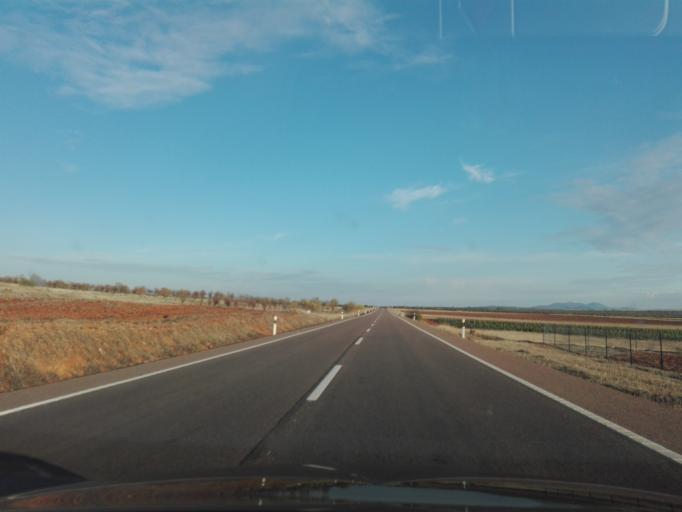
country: ES
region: Extremadura
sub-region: Provincia de Badajoz
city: Usagre
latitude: 38.3561
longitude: -6.2075
